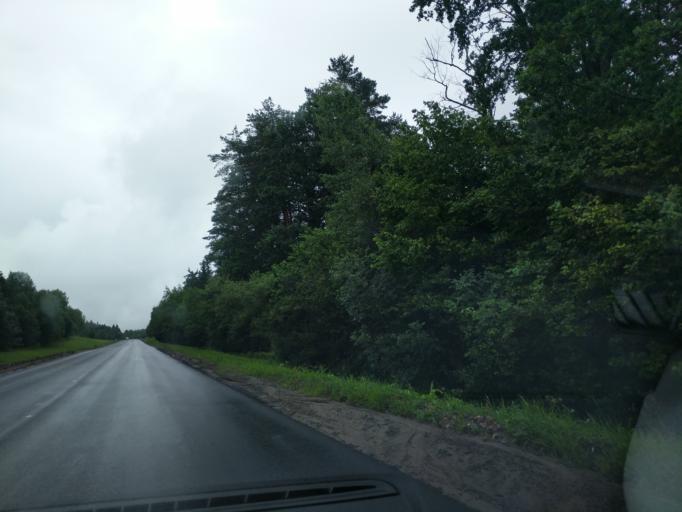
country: BY
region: Minsk
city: Syomkava
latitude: 54.2409
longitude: 27.4852
